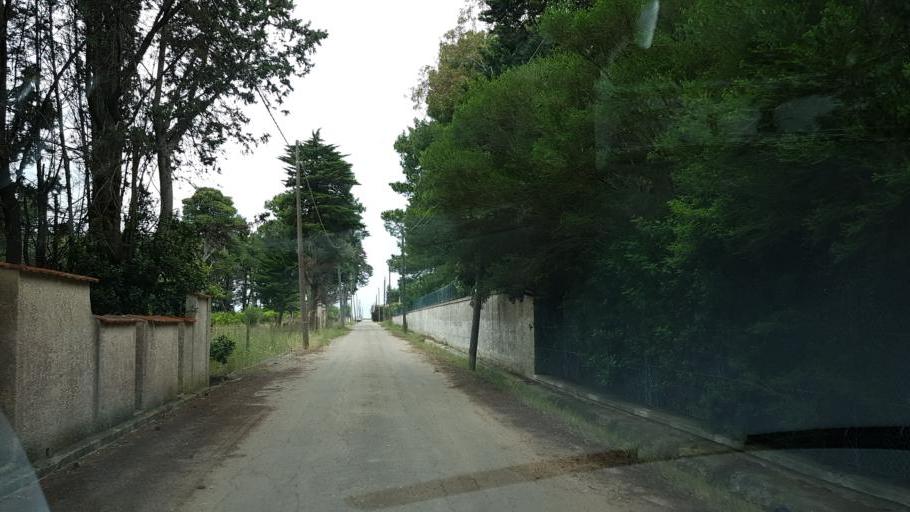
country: IT
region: Apulia
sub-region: Provincia di Brindisi
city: Brindisi
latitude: 40.6356
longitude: 17.8968
